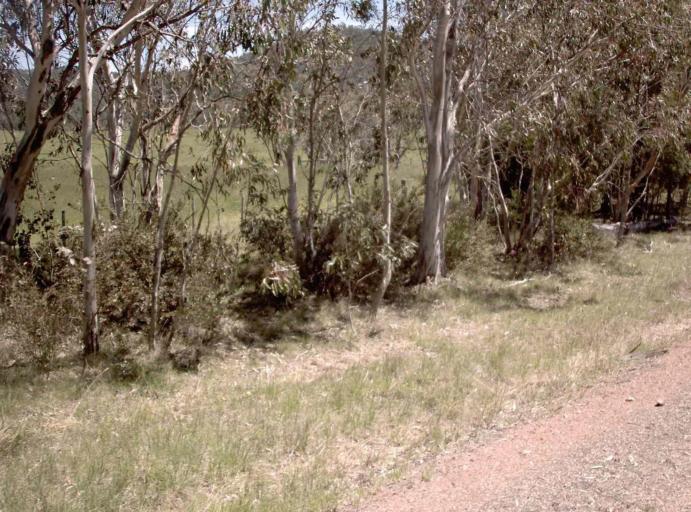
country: AU
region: New South Wales
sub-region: Snowy River
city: Jindabyne
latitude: -37.0744
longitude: 148.2599
